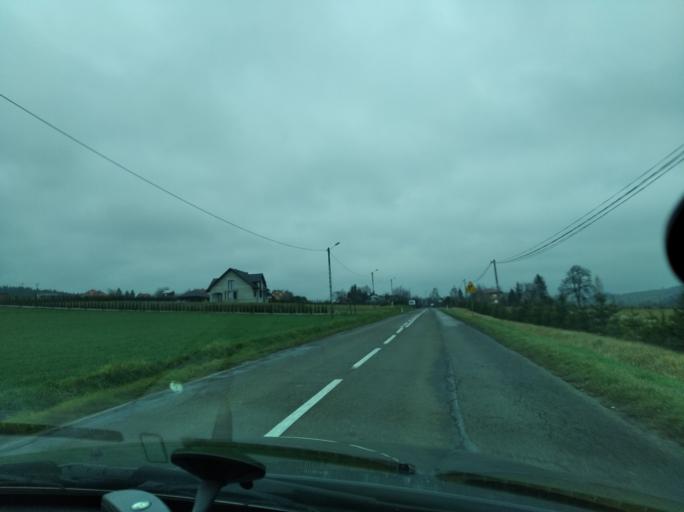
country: PL
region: Subcarpathian Voivodeship
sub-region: Powiat rzeszowski
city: Dynow
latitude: 49.8606
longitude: 22.2483
